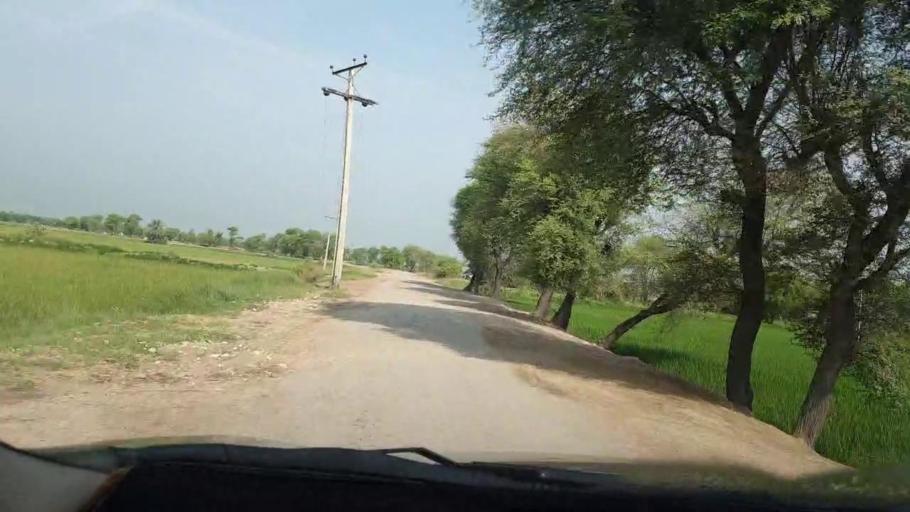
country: PK
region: Sindh
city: Goth Garelo
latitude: 27.4494
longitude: 68.0261
